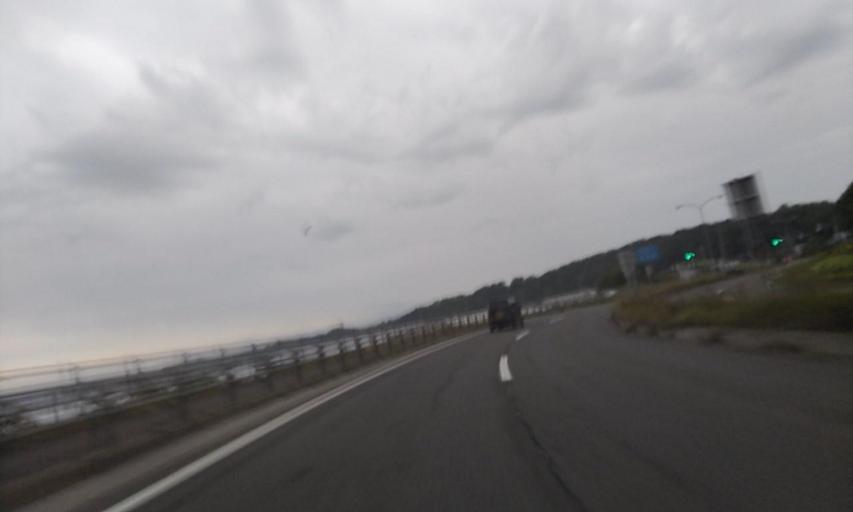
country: JP
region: Hokkaido
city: Abashiri
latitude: 43.9921
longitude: 144.2971
